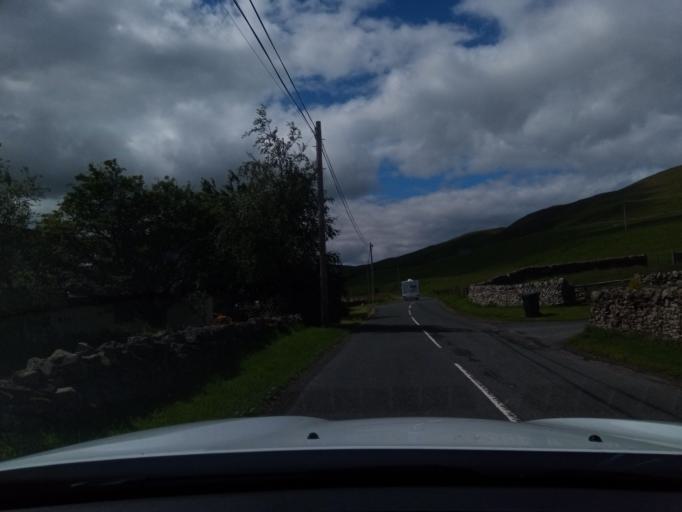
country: GB
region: Scotland
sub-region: The Scottish Borders
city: Innerleithen
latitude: 55.5450
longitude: -2.9966
